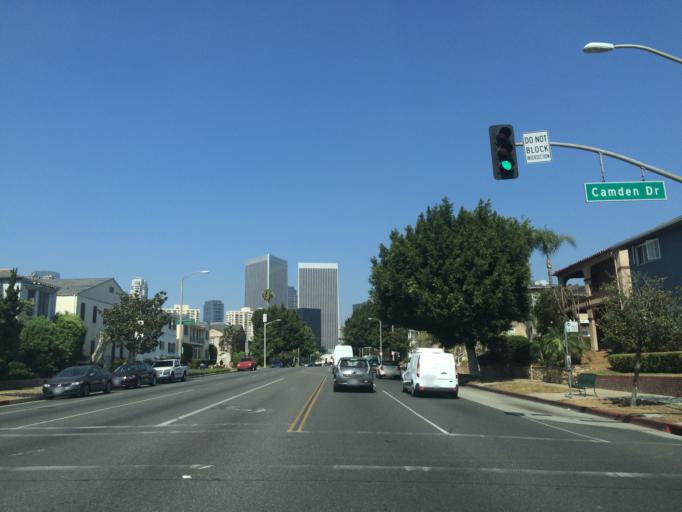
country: US
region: California
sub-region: Los Angeles County
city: Beverly Hills
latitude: 34.0597
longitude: -118.4023
